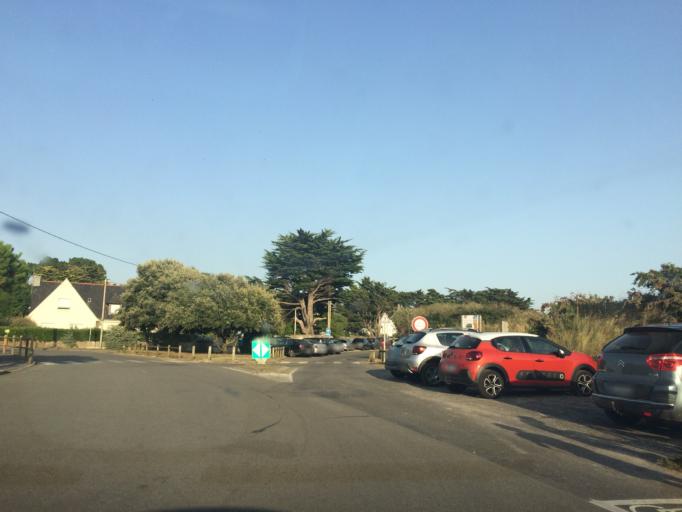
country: FR
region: Brittany
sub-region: Departement du Morbihan
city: Damgan
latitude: 47.5130
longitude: -2.5558
